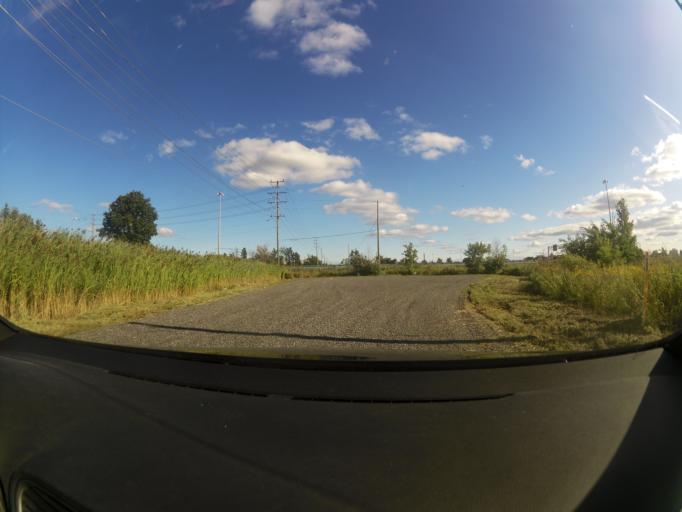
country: CA
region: Ontario
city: Bells Corners
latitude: 45.3047
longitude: -75.9168
